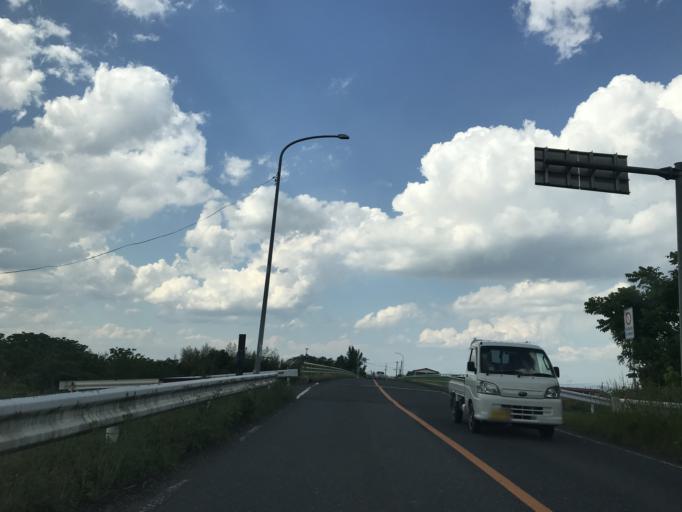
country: JP
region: Miyagi
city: Wakuya
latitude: 38.5974
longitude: 141.1684
